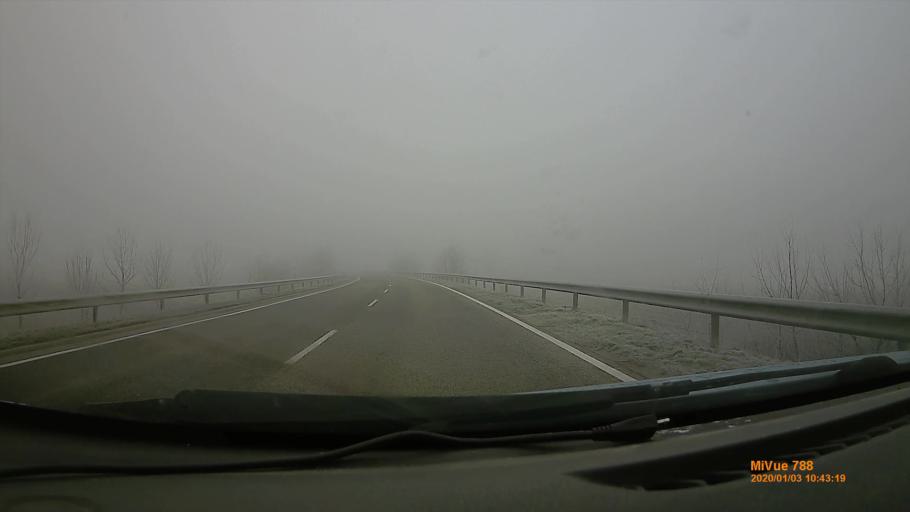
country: HU
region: Tolna
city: Bataszek
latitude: 46.2059
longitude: 18.7119
